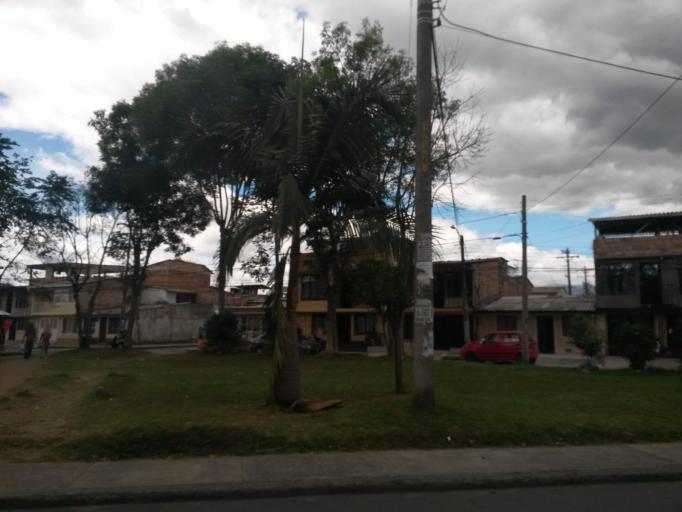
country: CO
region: Cauca
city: Popayan
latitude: 2.4386
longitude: -76.6189
